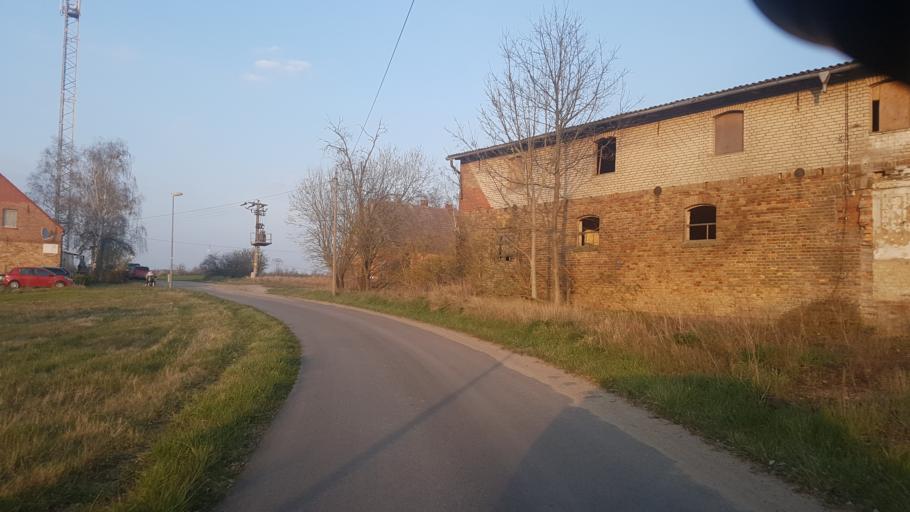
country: DE
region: Brandenburg
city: Gramzow
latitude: 53.2091
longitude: 13.9514
